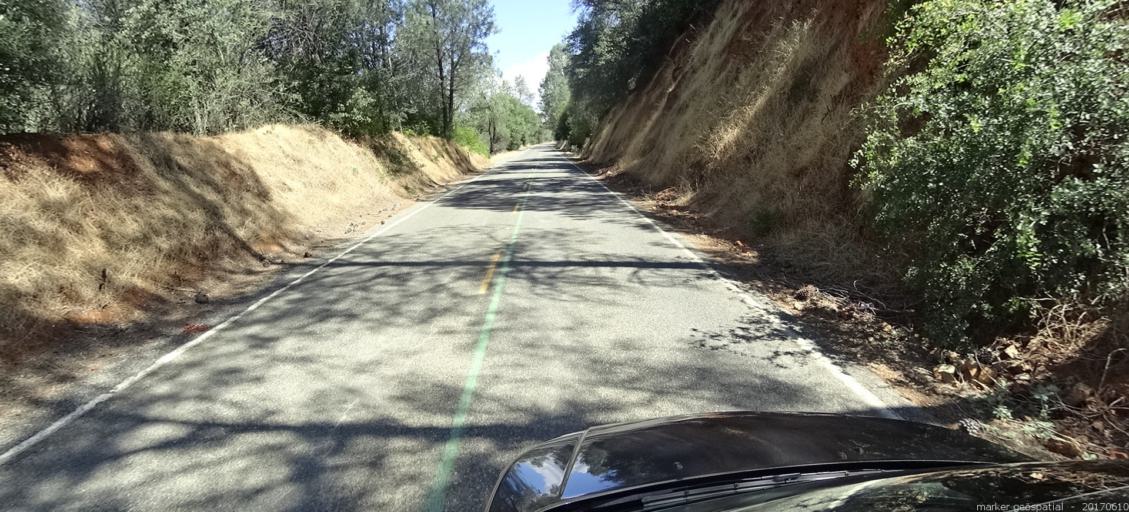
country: US
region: California
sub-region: Butte County
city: Oroville East
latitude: 39.5267
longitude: -121.5074
